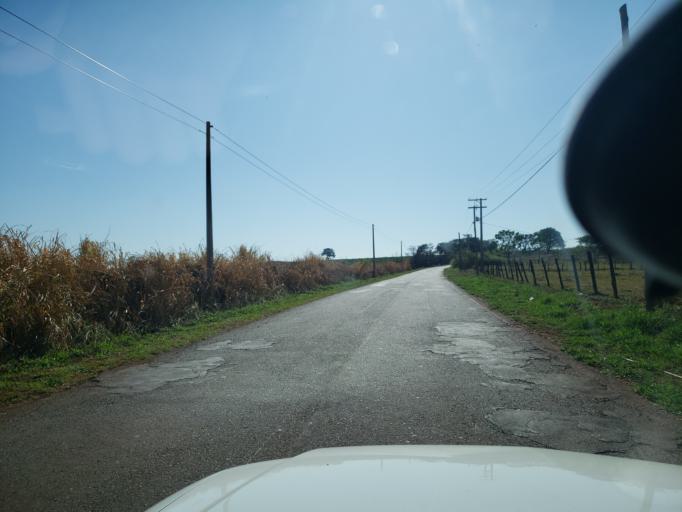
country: BR
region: Sao Paulo
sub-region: Moji-Guacu
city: Mogi-Gaucu
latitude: -22.3450
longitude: -46.8915
